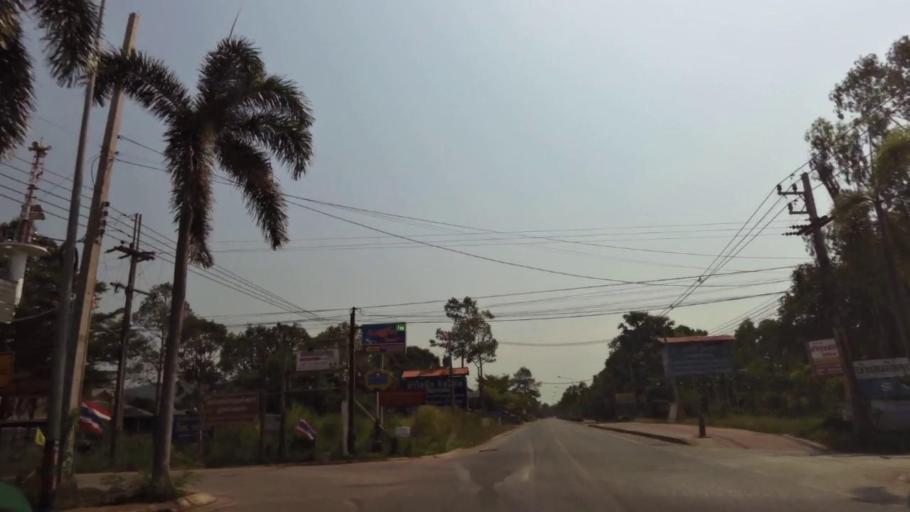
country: TH
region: Chanthaburi
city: Tha Mai
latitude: 12.5502
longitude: 101.9254
